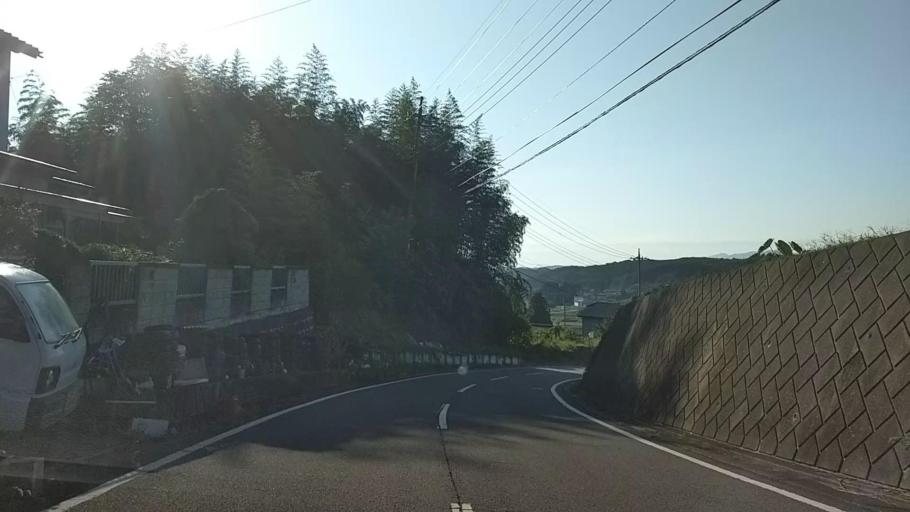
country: JP
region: Gunma
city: Annaka
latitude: 36.3556
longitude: 138.8571
